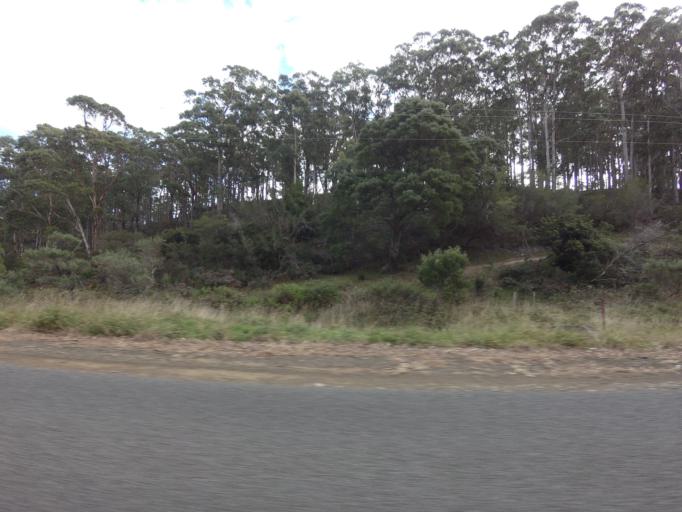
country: AU
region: Tasmania
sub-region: Clarence
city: Sandford
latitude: -43.0788
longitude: 147.7463
